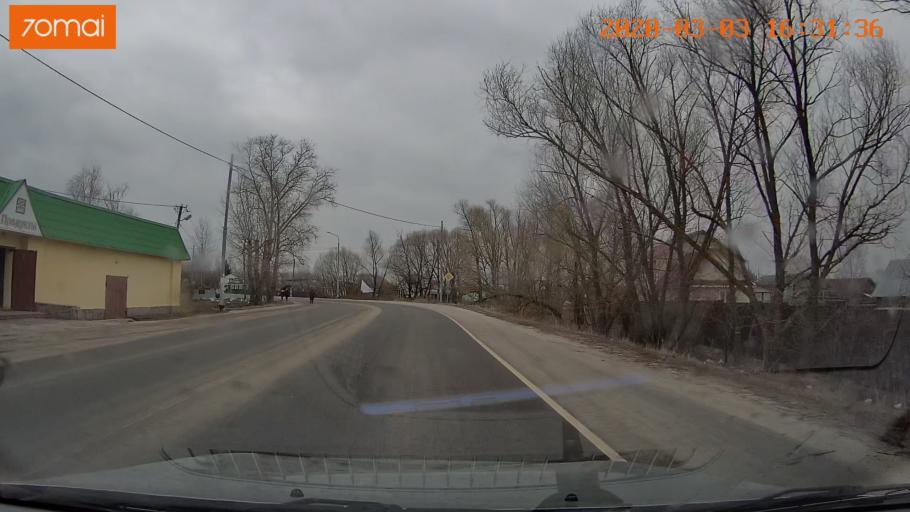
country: RU
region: Moskovskaya
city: Konobeyevo
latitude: 55.4242
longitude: 38.7266
